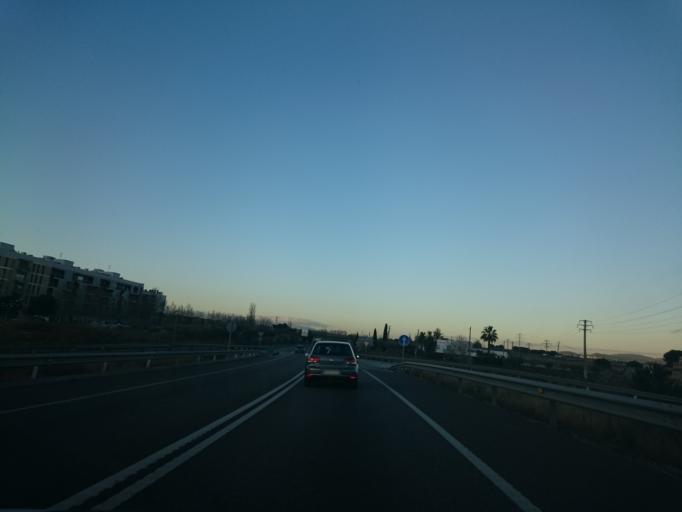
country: ES
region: Catalonia
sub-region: Provincia de Barcelona
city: Vilafranca del Penedes
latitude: 41.3371
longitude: 1.7071
